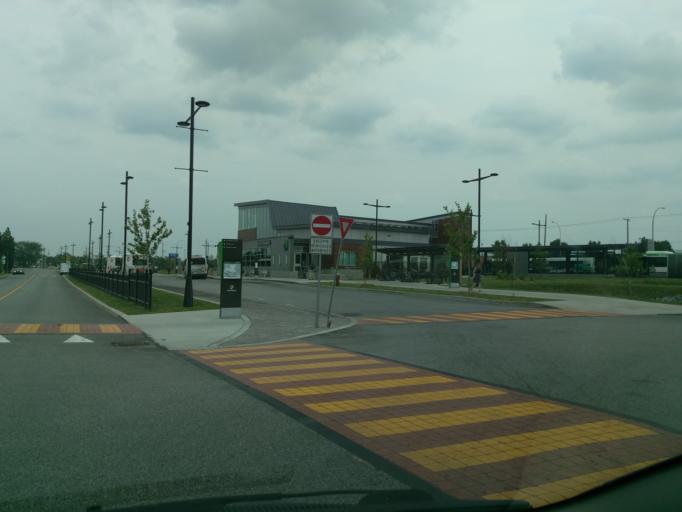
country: CA
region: Quebec
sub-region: Outaouais
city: Gatineau
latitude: 45.4816
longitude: -75.6849
